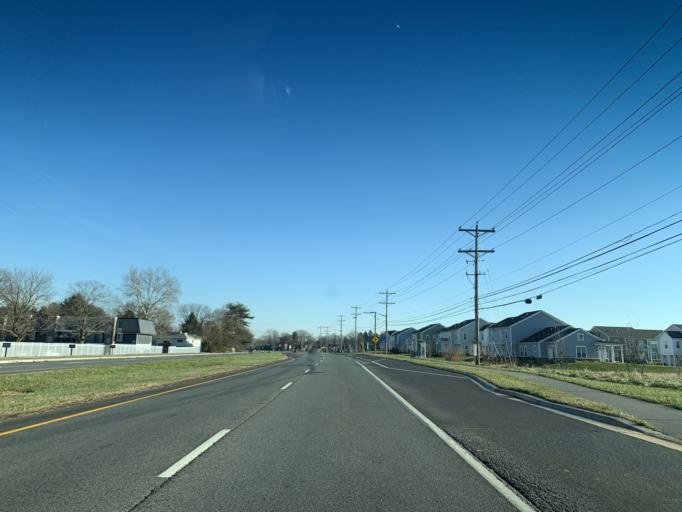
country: US
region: Delaware
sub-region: New Castle County
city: Brookside
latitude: 39.6656
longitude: -75.7186
